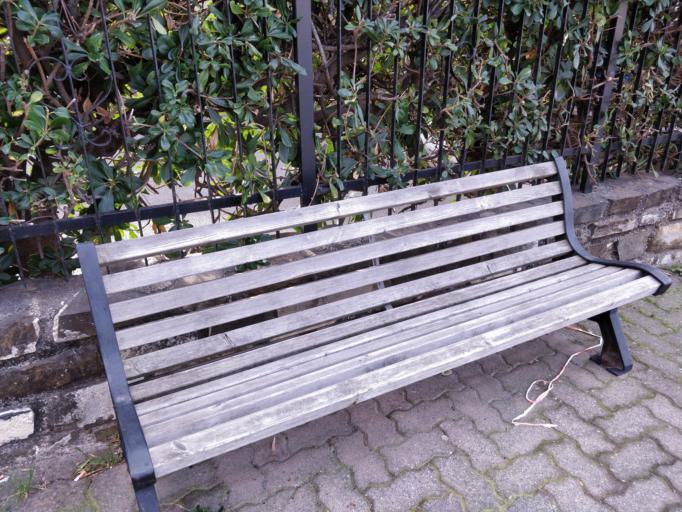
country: IT
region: Liguria
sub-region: Provincia di Savona
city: Andora
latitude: 43.9517
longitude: 8.1437
